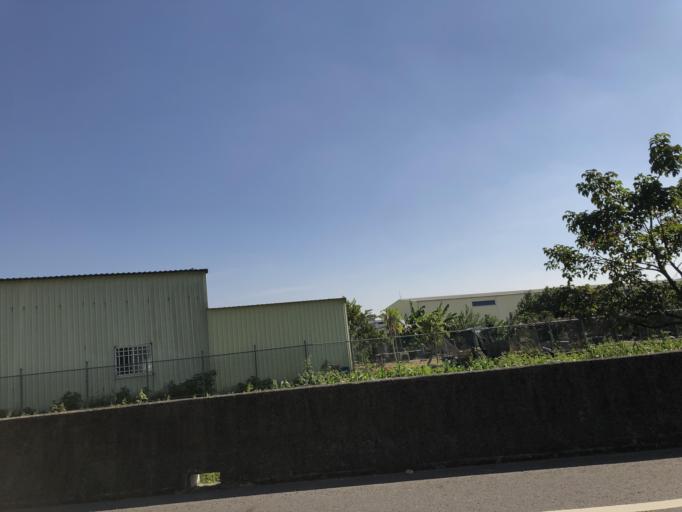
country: TW
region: Taiwan
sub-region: Tainan
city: Tainan
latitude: 23.0077
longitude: 120.2863
